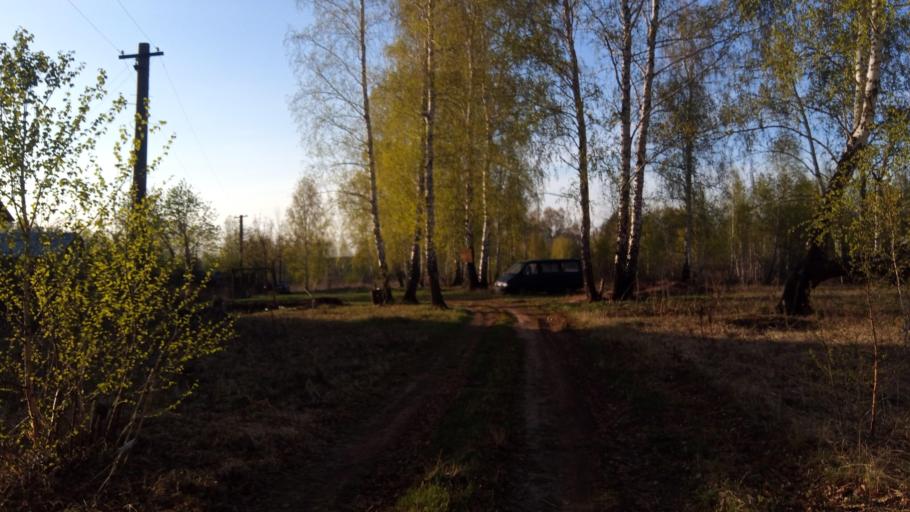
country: RU
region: Chelyabinsk
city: Timiryazevskiy
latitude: 54.9931
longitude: 60.8452
